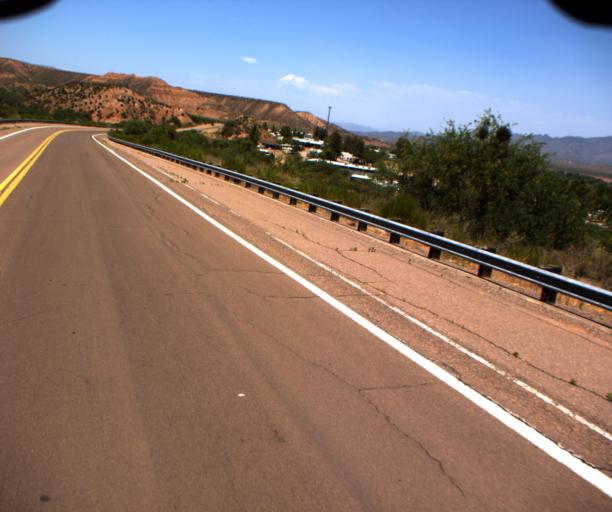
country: US
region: Arizona
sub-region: Gila County
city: Tonto Basin
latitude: 33.8707
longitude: -111.3152
